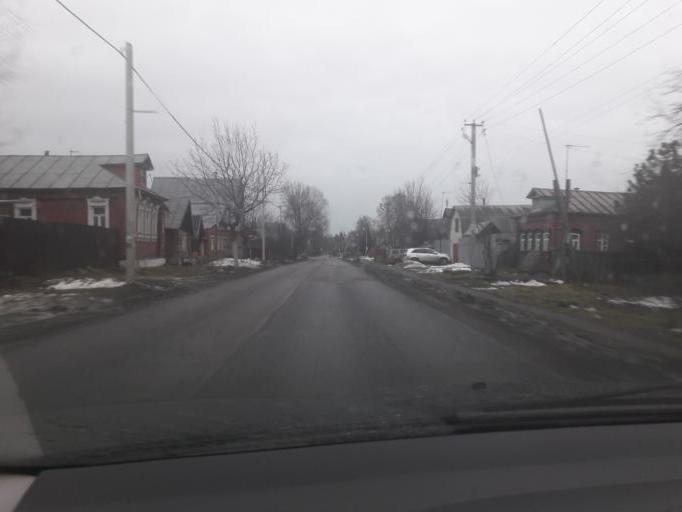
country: RU
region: Moskovskaya
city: Fryazevo
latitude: 55.7507
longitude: 38.5318
